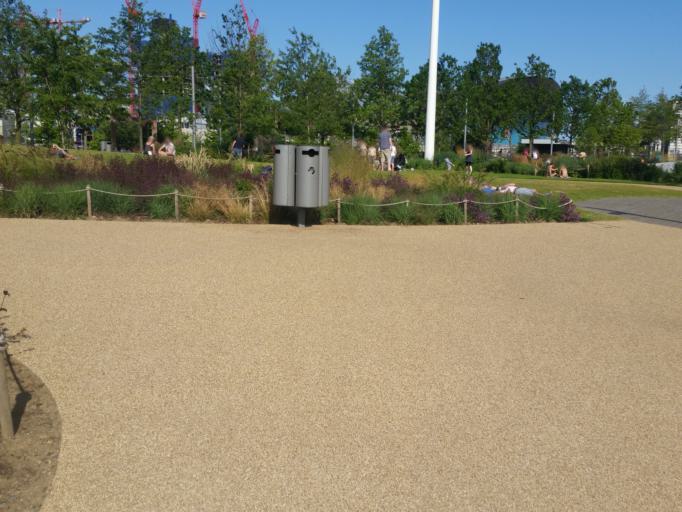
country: GB
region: England
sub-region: Greater London
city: Poplar
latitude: 51.5406
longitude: -0.0148
